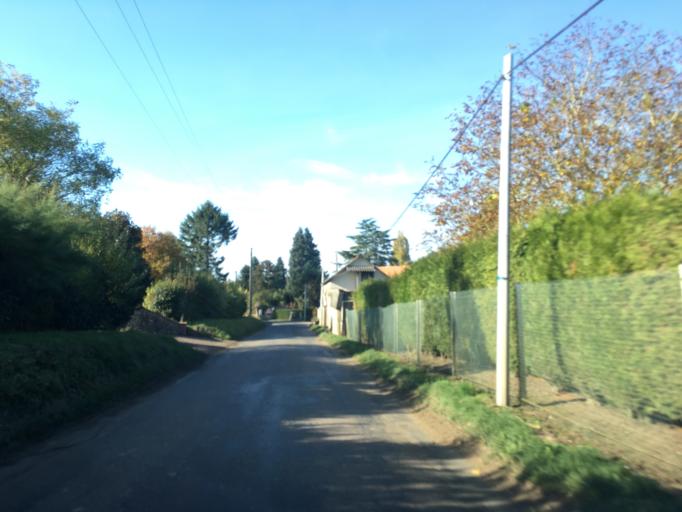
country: FR
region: Haute-Normandie
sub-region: Departement de l'Eure
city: Heudreville-sur-Eure
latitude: 49.1604
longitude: 1.2510
